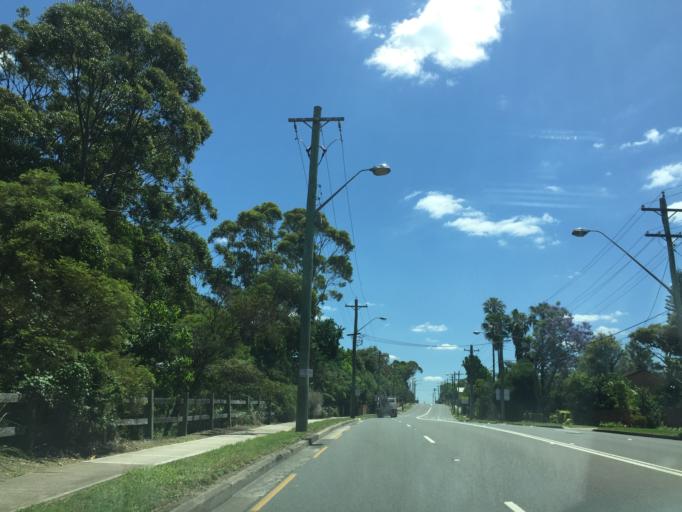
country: AU
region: New South Wales
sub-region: Parramatta
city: Dundas Valley
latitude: -33.7830
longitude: 151.0575
